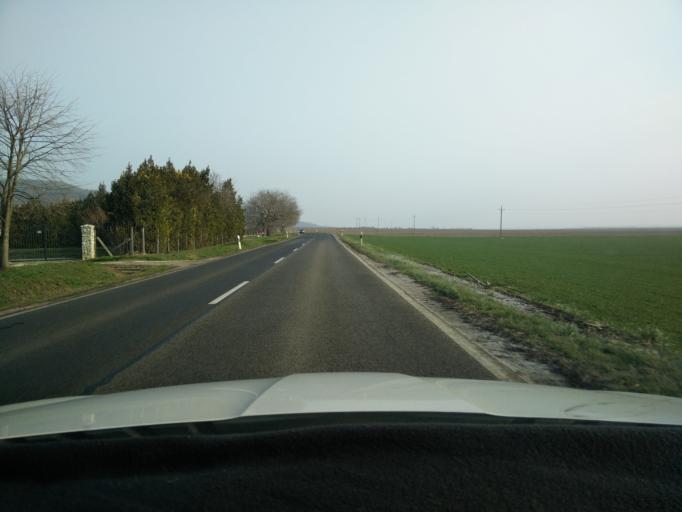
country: HU
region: Tolna
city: Szekszard
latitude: 46.2896
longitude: 18.6858
